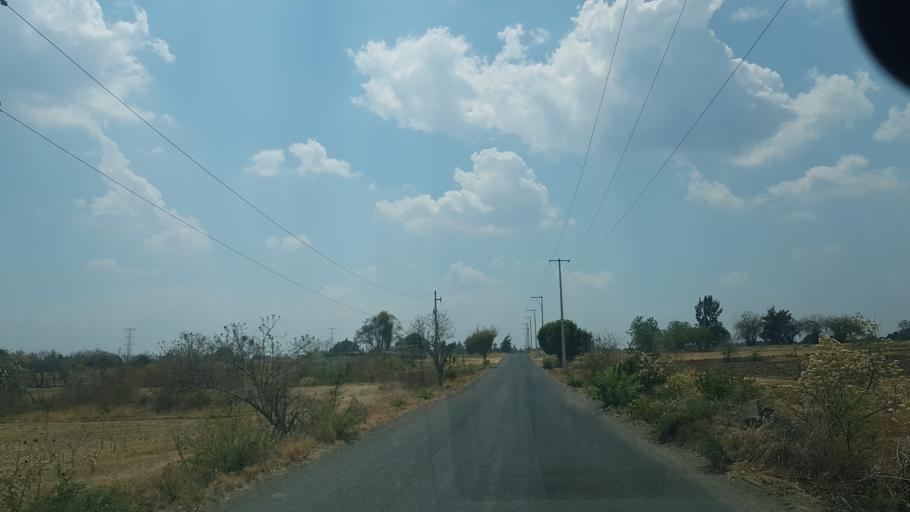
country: MX
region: Puebla
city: San Juan Amecac
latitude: 18.8287
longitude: -98.6493
